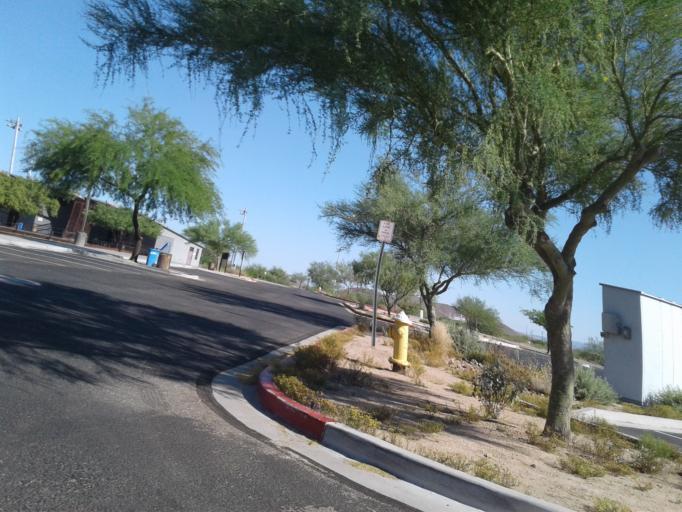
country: US
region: Arizona
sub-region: Maricopa County
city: Cave Creek
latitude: 33.6840
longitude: -112.0266
